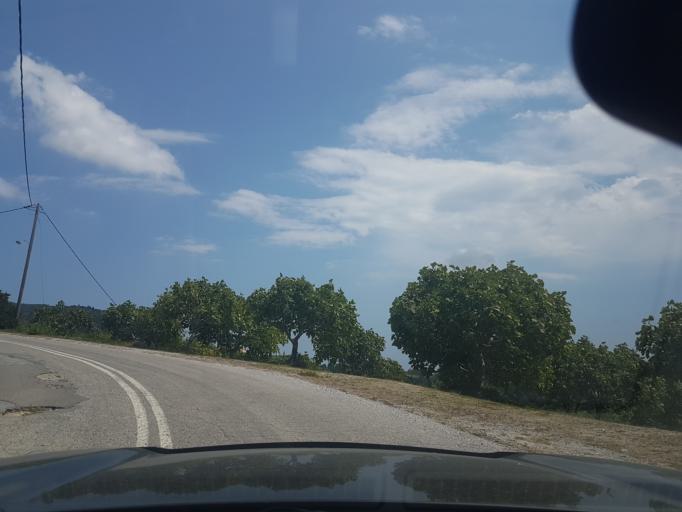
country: GR
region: Central Greece
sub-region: Nomos Evvoias
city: Kymi
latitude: 38.6459
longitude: 24.0386
